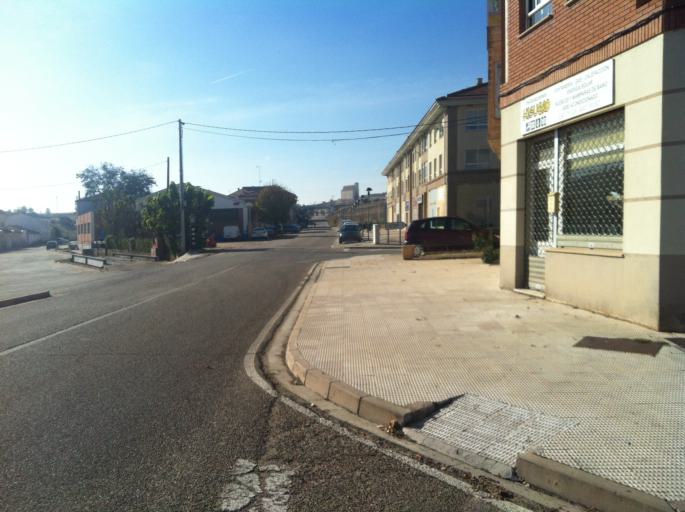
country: ES
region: Castille and Leon
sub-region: Provincia de Burgos
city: Lerma
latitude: 42.0255
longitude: -3.7626
